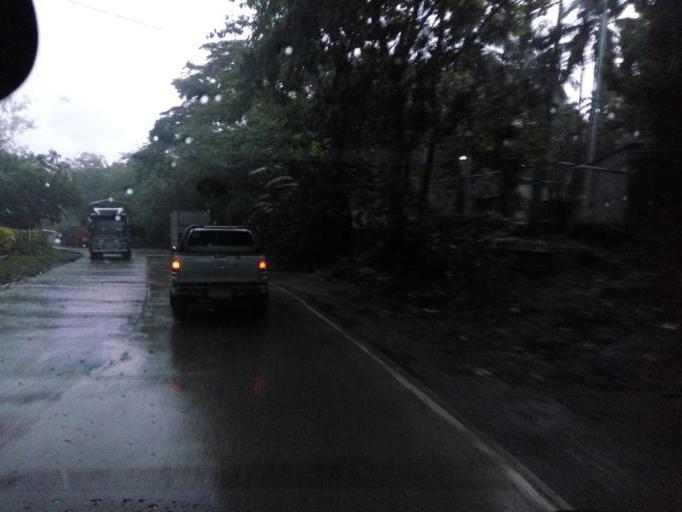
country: PH
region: Cagayan Valley
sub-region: Province of Nueva Vizcaya
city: Santa Fe
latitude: 16.1562
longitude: 120.9369
